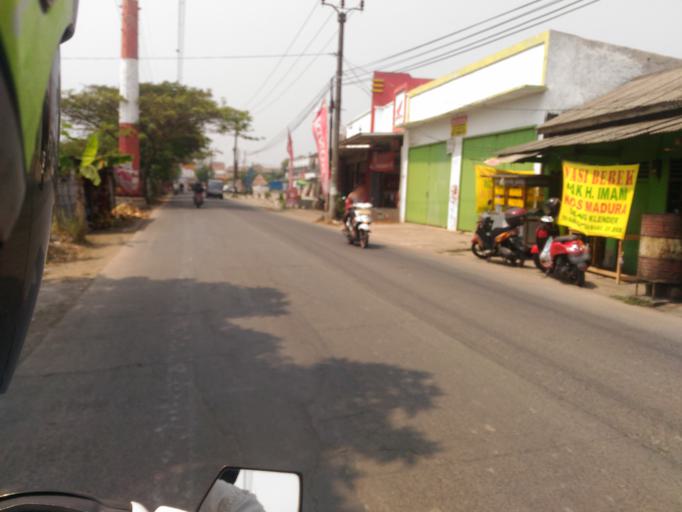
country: ID
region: West Java
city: Sepatan
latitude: -6.1481
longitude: 106.5832
